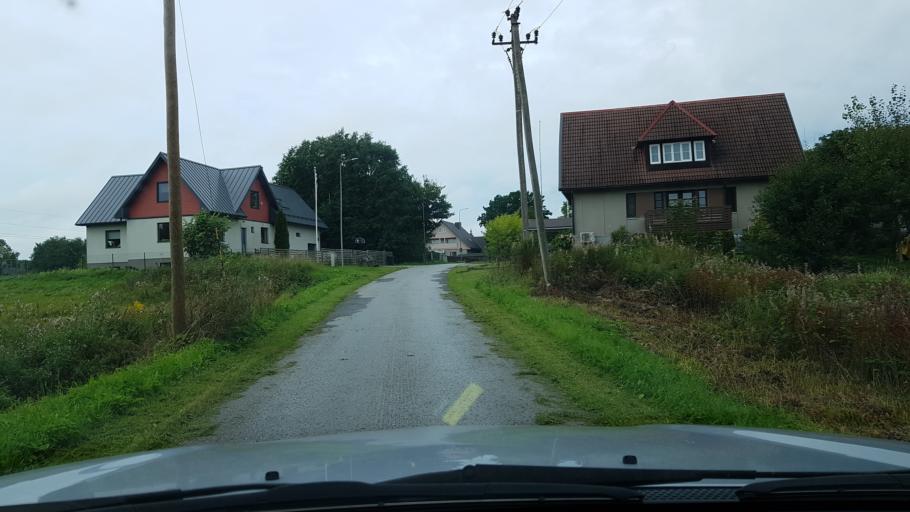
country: EE
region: Harju
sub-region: Rae vald
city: Jueri
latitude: 59.3542
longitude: 24.9243
